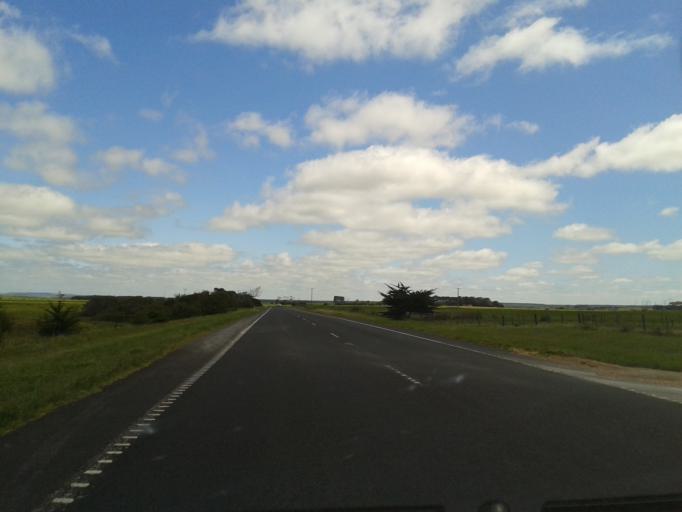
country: AU
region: Victoria
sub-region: Moyne
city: Port Fairy
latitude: -38.2608
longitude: 141.9351
